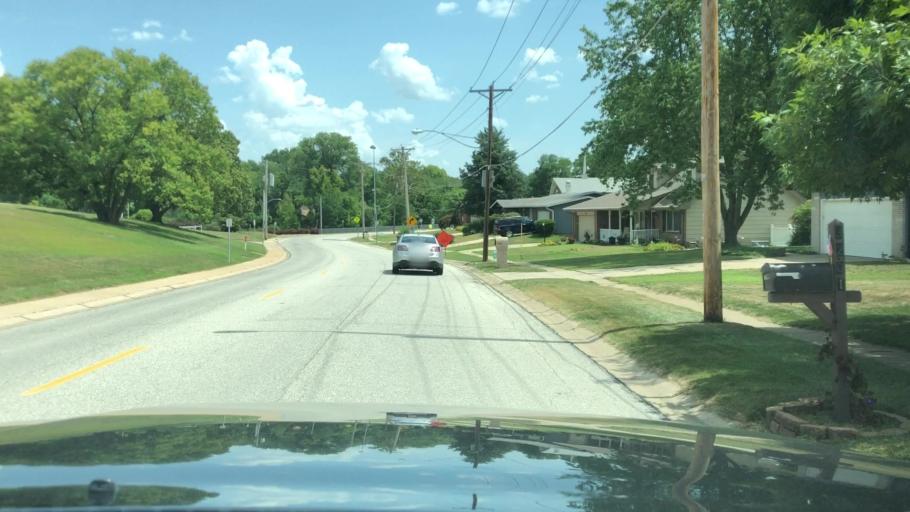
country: US
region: Missouri
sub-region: Saint Charles County
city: Saint Charles
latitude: 38.7983
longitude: -90.5274
